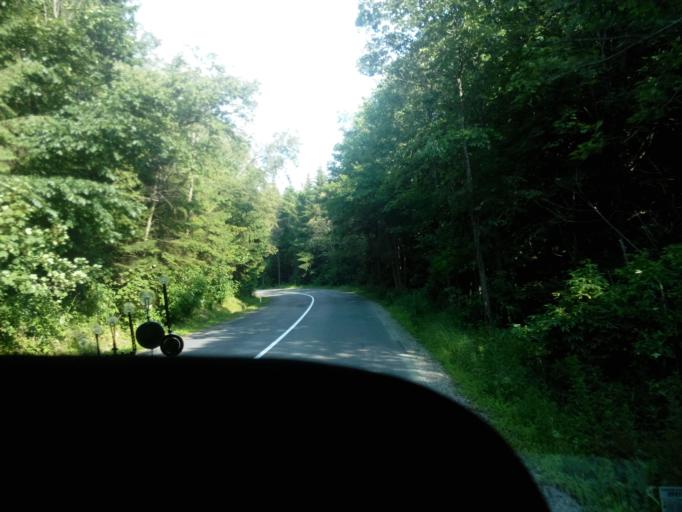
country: RO
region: Brasov
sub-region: Oras Predeal
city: Predeal
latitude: 45.5180
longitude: 25.5024
